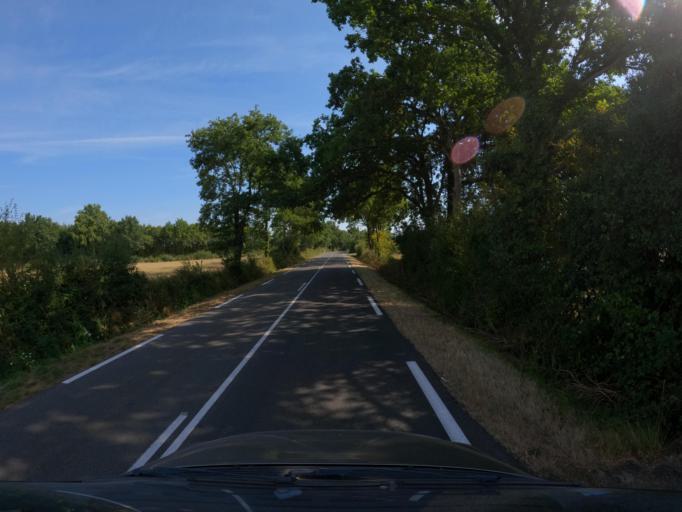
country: FR
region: Pays de la Loire
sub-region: Departement de la Vendee
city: Saint-Christophe-du-Ligneron
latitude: 46.8389
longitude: -1.7510
